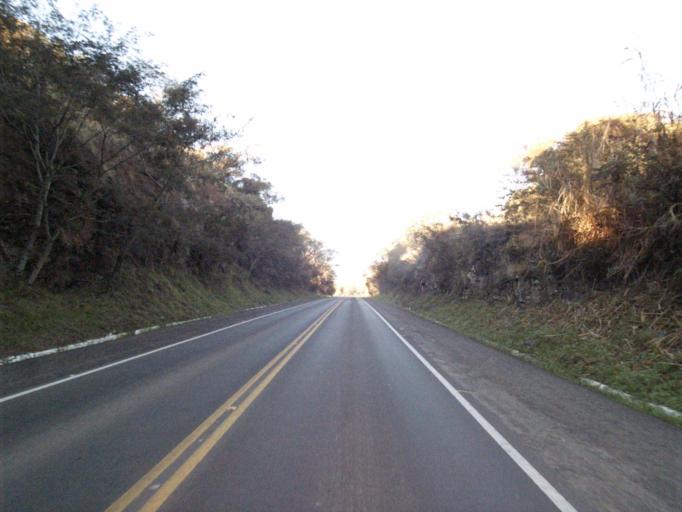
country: BR
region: Rio Grande do Sul
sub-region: Frederico Westphalen
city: Frederico Westphalen
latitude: -26.7780
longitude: -53.2760
